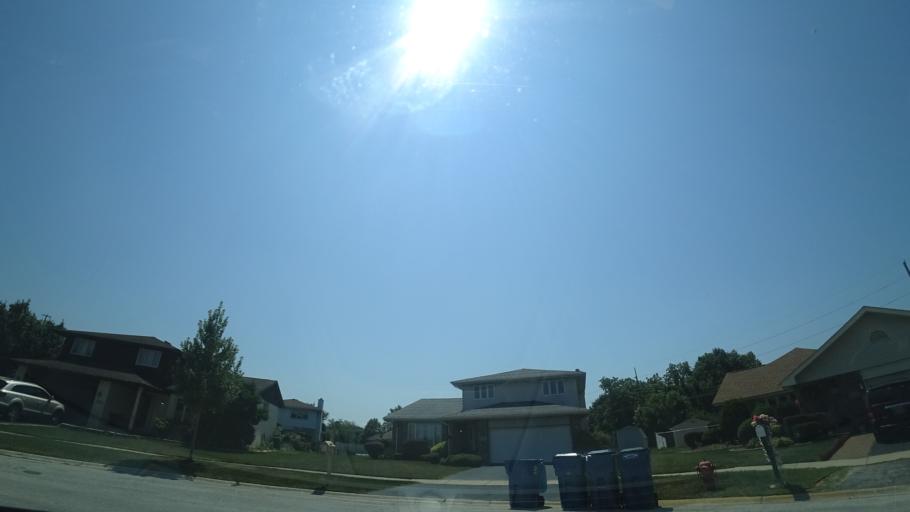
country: US
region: Illinois
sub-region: Cook County
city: Alsip
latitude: 41.6859
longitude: -87.7426
